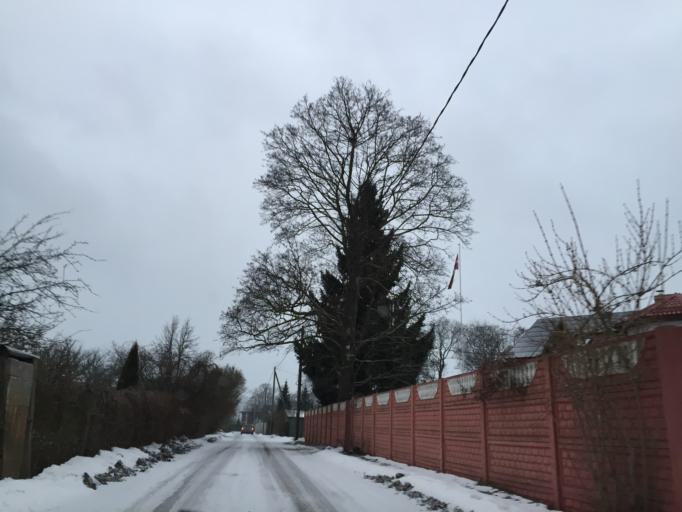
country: LV
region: Riga
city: Riga
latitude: 56.9221
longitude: 24.1286
